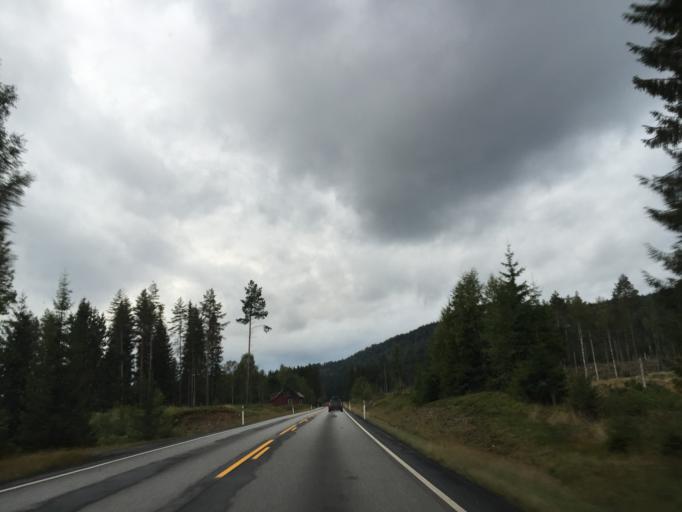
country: NO
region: Hedmark
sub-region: Nord-Odal
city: Sand
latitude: 60.4938
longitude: 11.5017
